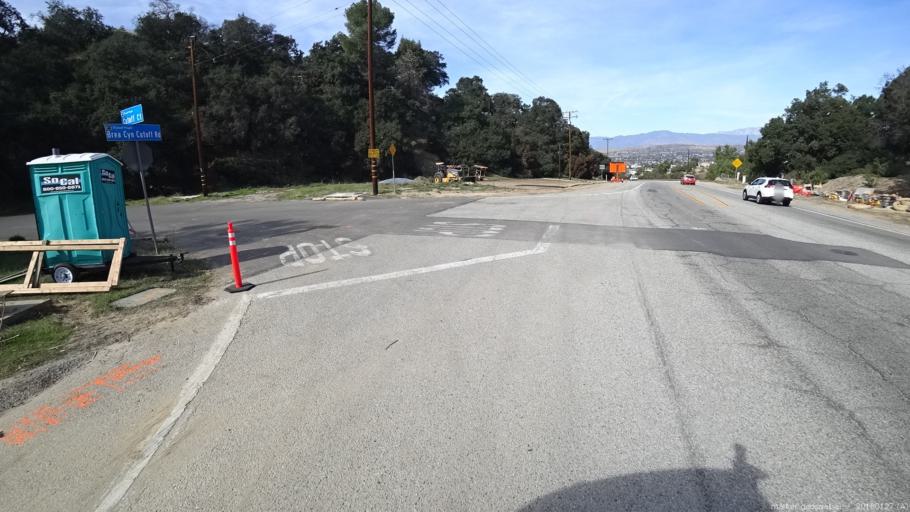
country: US
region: California
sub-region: Los Angeles County
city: Walnut
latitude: 33.9768
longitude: -117.8597
